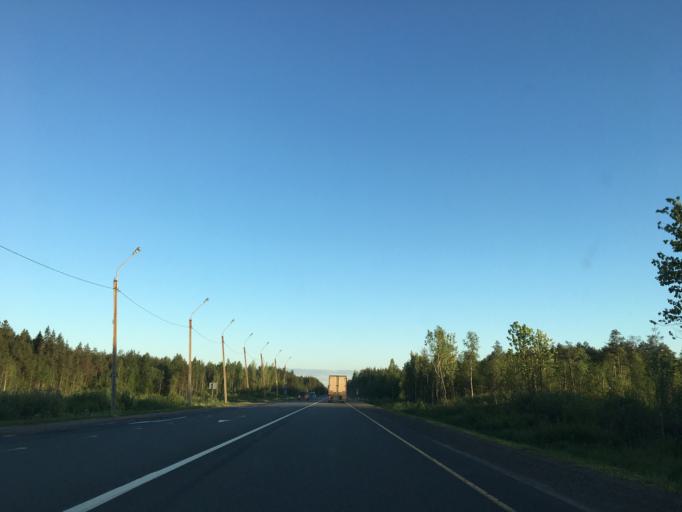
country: RU
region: Leningrad
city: Rozhdestveno
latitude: 59.3012
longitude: 29.9417
